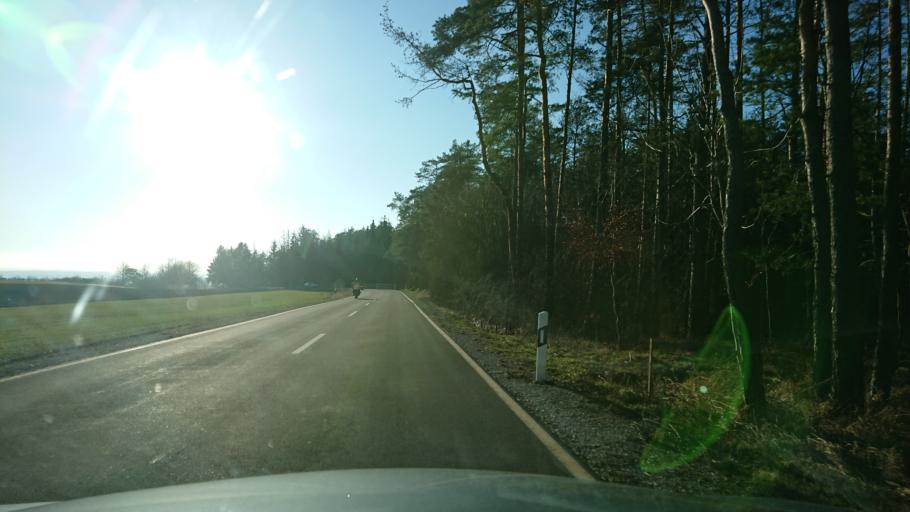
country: DE
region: Bavaria
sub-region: Upper Franconia
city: Weilersbach
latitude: 49.7961
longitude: 11.1319
